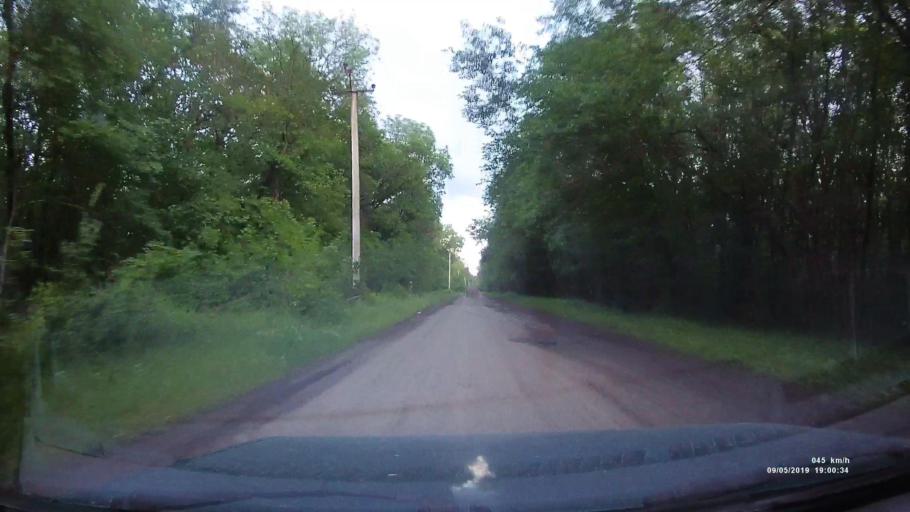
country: RU
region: Krasnodarskiy
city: Kanelovskaya
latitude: 46.7514
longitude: 39.1370
